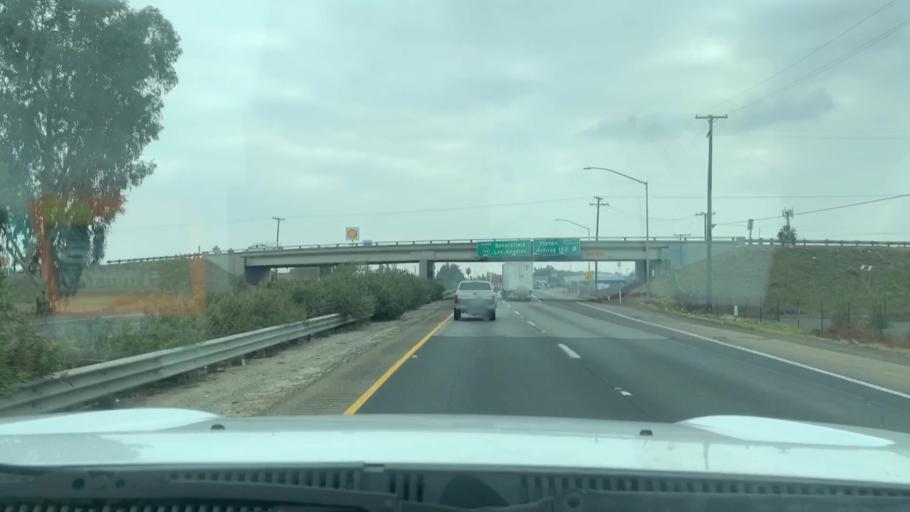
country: US
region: California
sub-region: Tulare County
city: Tipton
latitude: 36.0666
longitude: -119.3146
